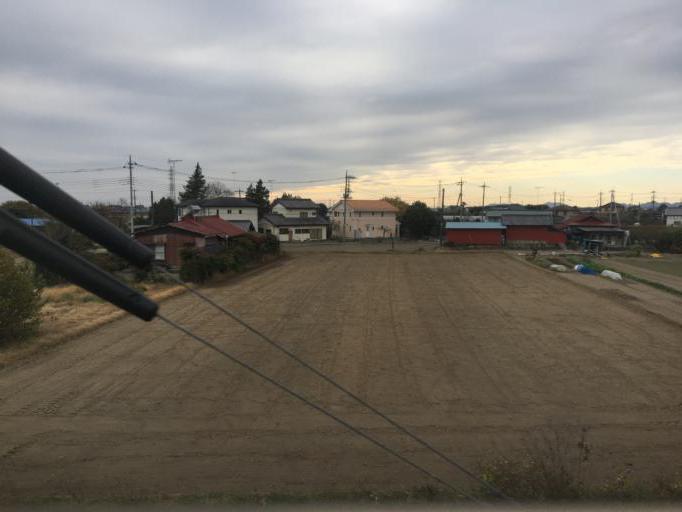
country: JP
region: Tochigi
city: Oyama
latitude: 36.3402
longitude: 139.8012
